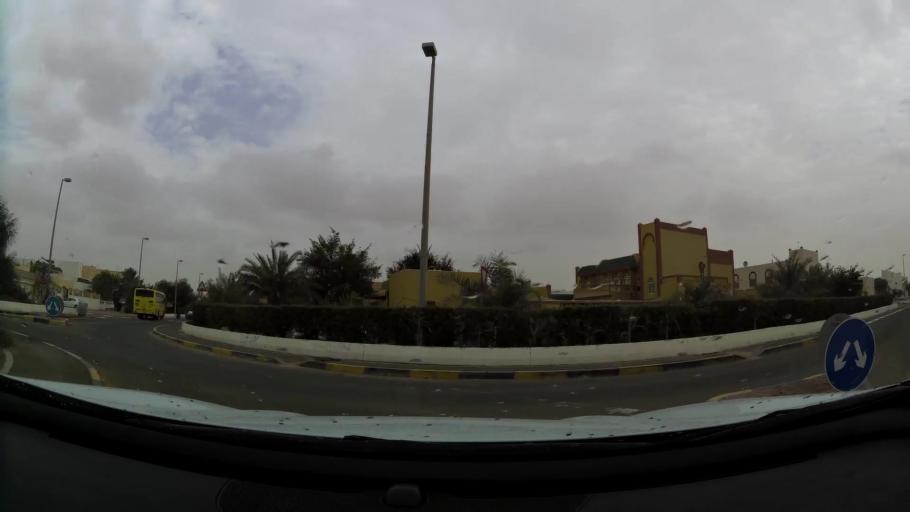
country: AE
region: Abu Dhabi
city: Abu Dhabi
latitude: 24.3314
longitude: 54.6357
